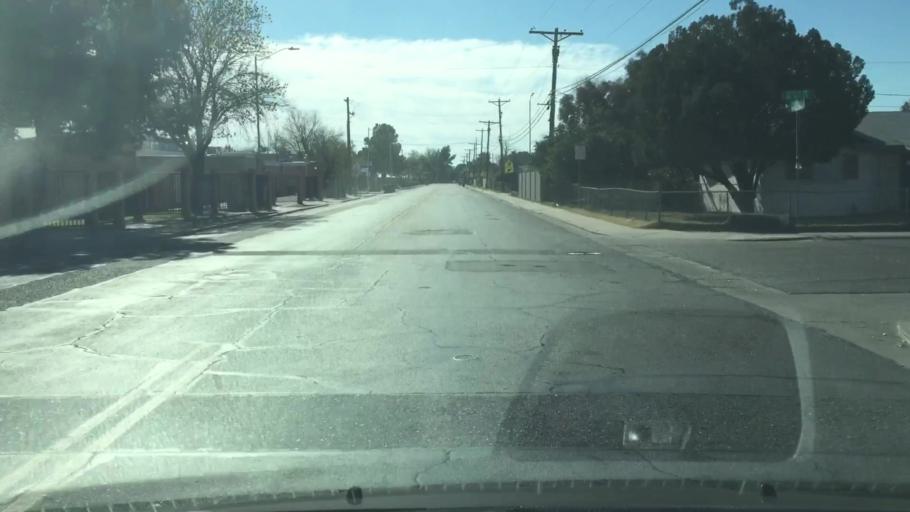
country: US
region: Arizona
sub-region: Maricopa County
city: Mesa
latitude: 33.4259
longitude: -111.8523
